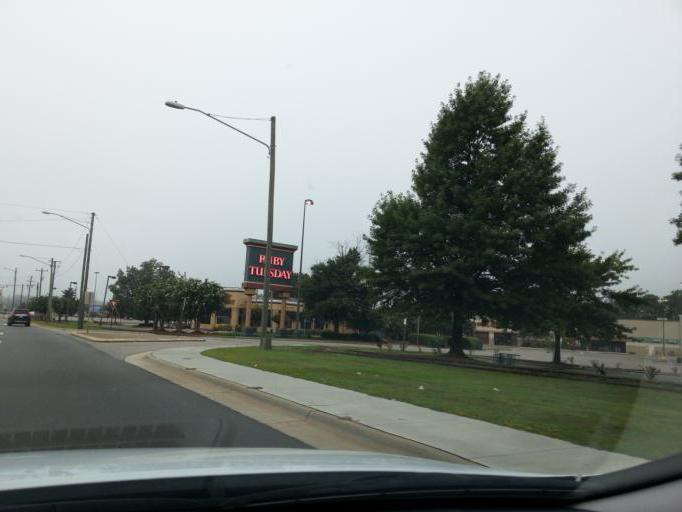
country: US
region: North Carolina
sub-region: Cumberland County
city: Fort Bragg
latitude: 35.0742
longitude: -78.9637
